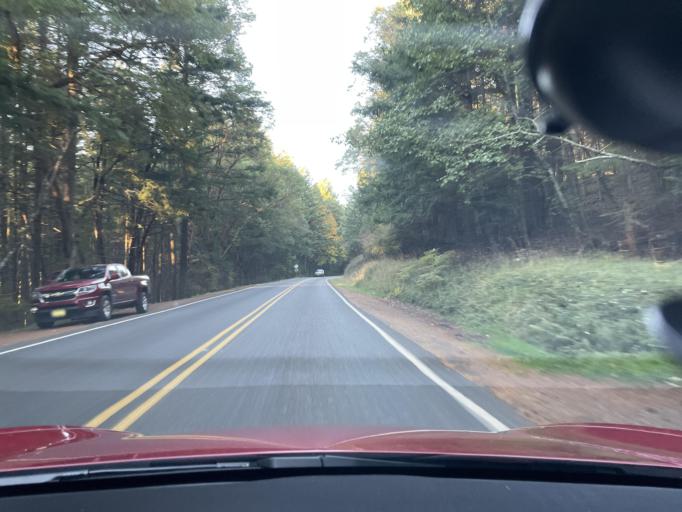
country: US
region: Washington
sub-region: San Juan County
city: Friday Harbor
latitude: 48.5847
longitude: -123.1441
